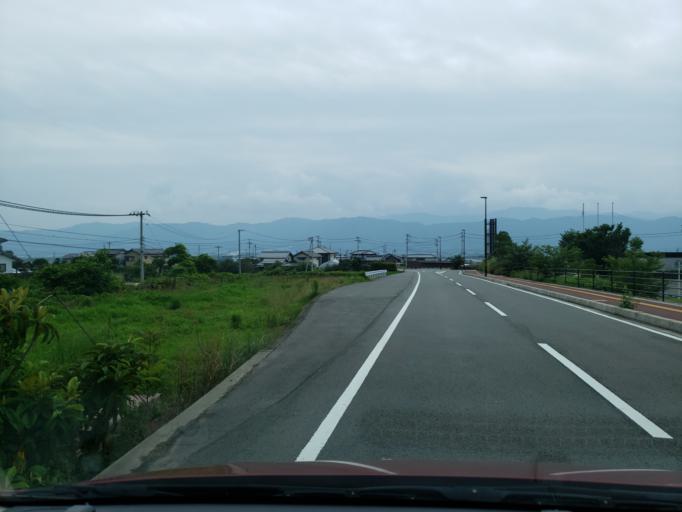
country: JP
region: Tokushima
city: Kamojimacho-jogejima
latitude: 34.1026
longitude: 134.2983
